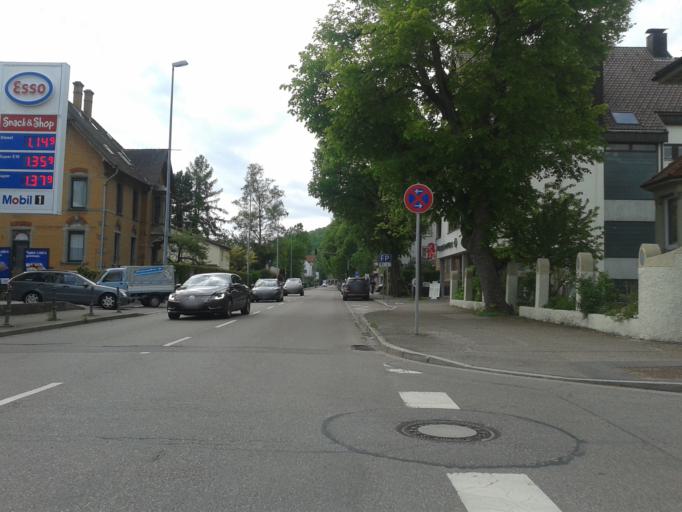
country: DE
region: Baden-Wuerttemberg
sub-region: Tuebingen Region
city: Blaubeuren
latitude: 48.4082
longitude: 9.7874
